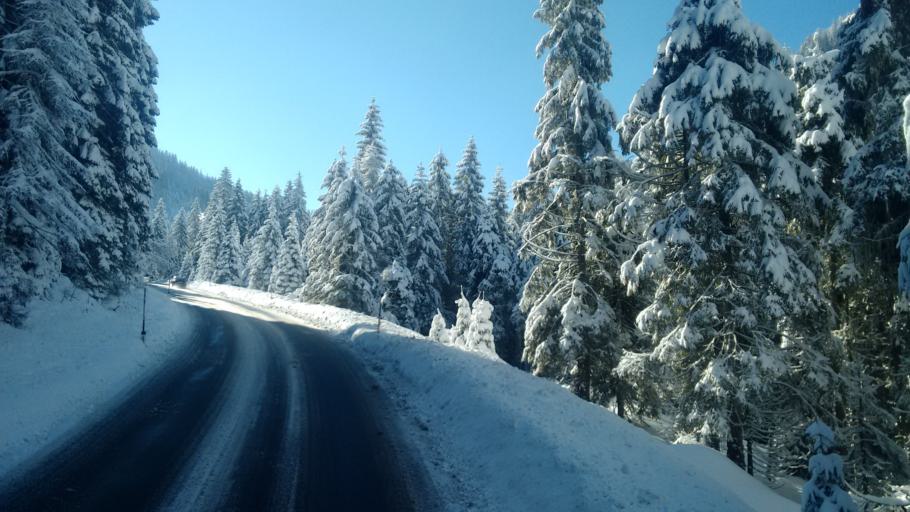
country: AT
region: Salzburg
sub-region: Politischer Bezirk Sankt Johann im Pongau
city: Untertauern
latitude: 47.3055
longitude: 13.4527
